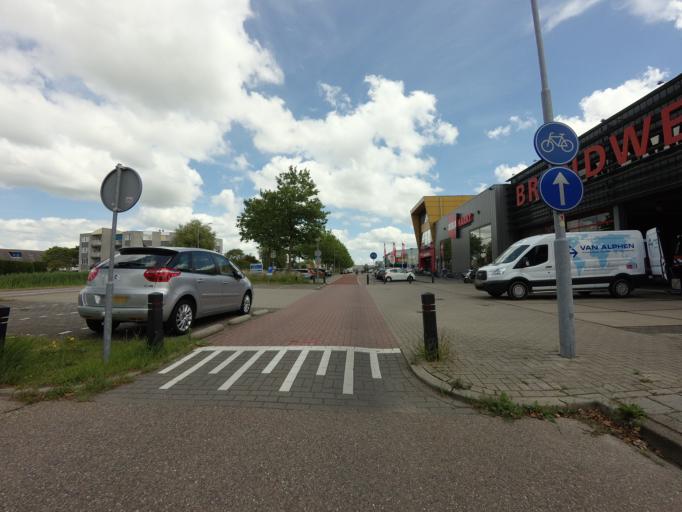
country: NL
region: North Holland
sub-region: Gemeente Zaanstad
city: Zaanstad
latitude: 52.4905
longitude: 4.8090
